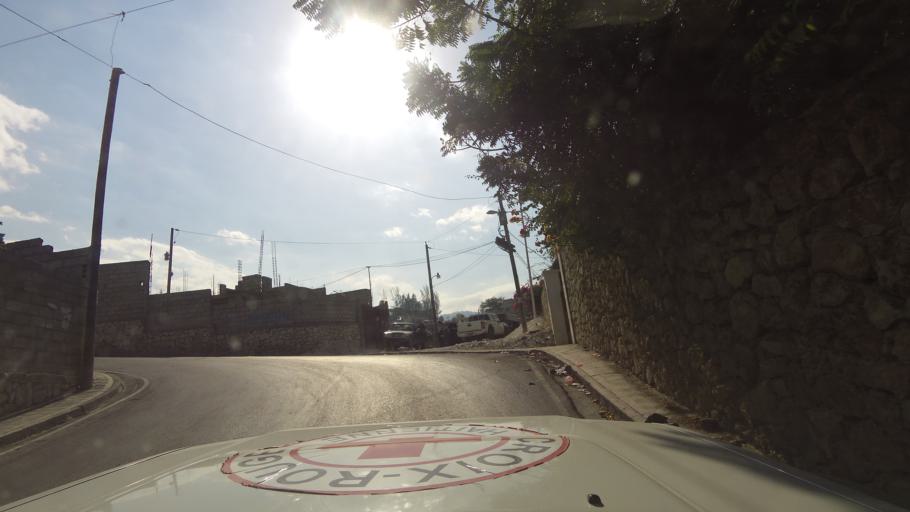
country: HT
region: Ouest
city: Petionville
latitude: 18.5207
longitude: -72.2740
